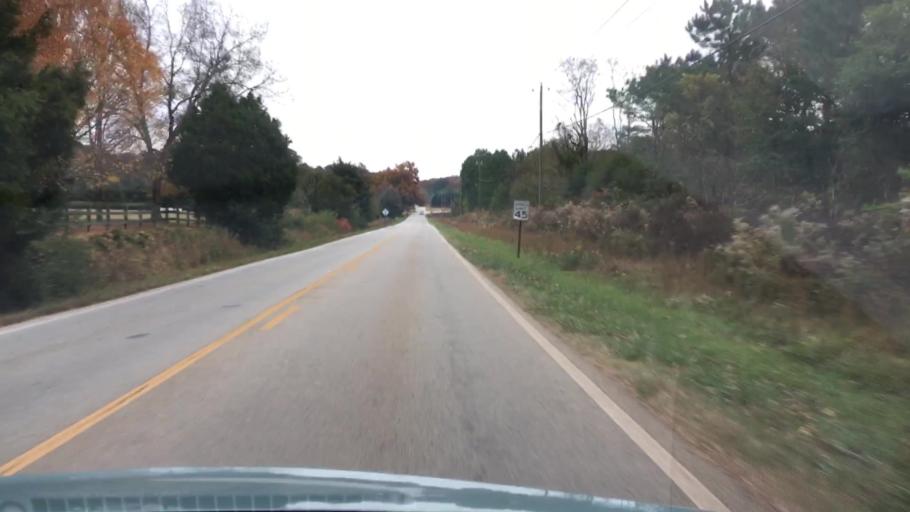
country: US
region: Georgia
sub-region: Henry County
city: McDonough
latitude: 33.5074
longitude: -84.1135
